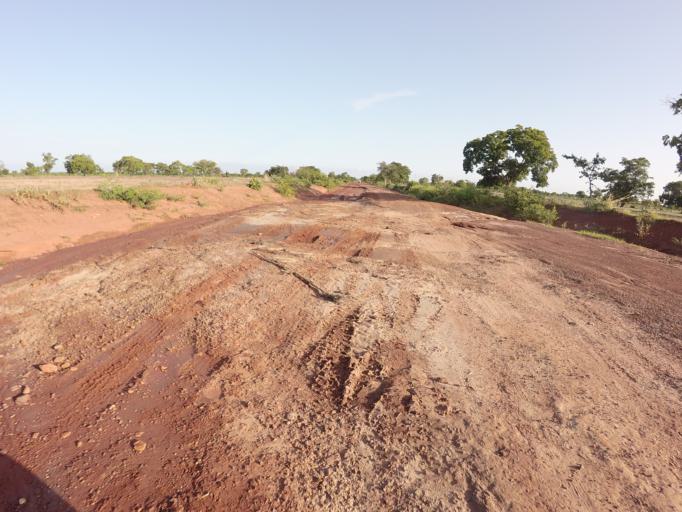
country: TG
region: Savanes
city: Sansanne-Mango
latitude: 10.3713
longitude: -0.0941
